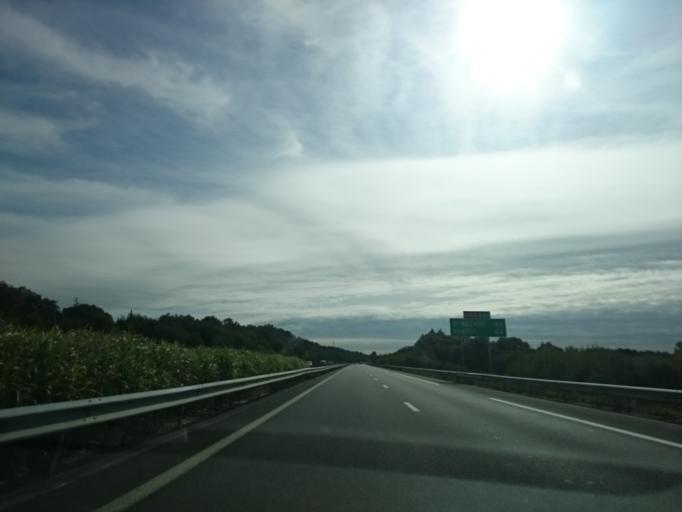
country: FR
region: Brittany
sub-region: Departement du Morbihan
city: Nivillac
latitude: 47.4979
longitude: -2.2555
